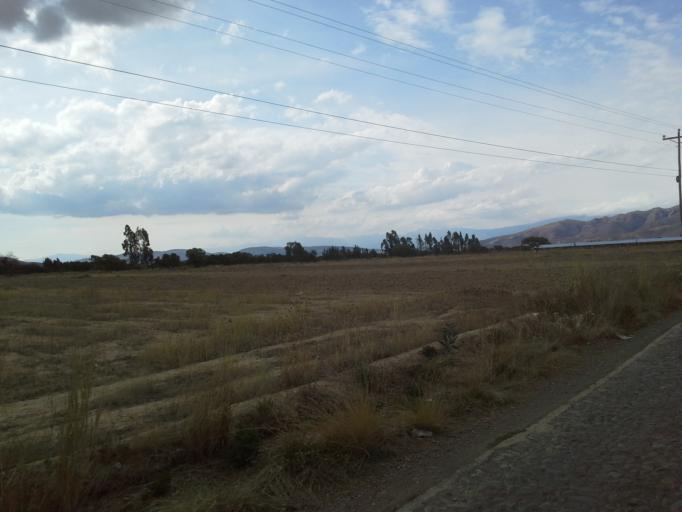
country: BO
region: Cochabamba
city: Tarata
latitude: -17.5951
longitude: -66.0186
